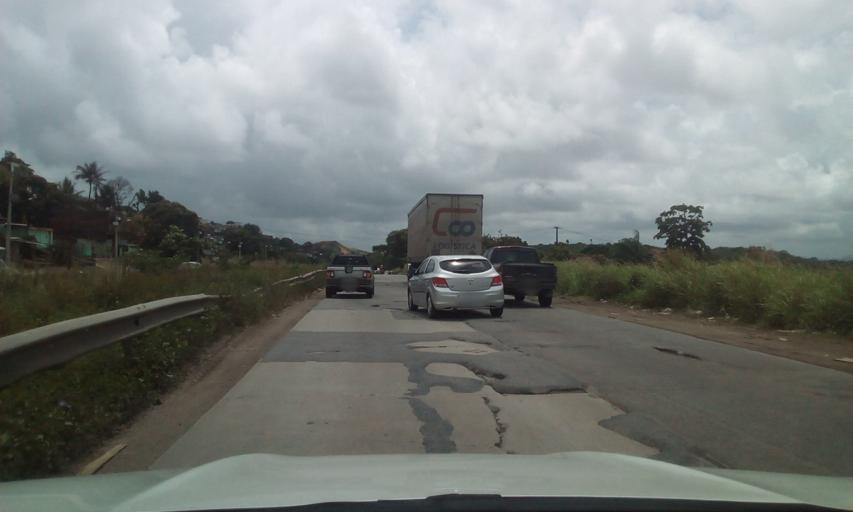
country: BR
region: Pernambuco
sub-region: Jaboatao Dos Guararapes
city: Jaboatao dos Guararapes
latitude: -8.1169
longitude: -34.9439
